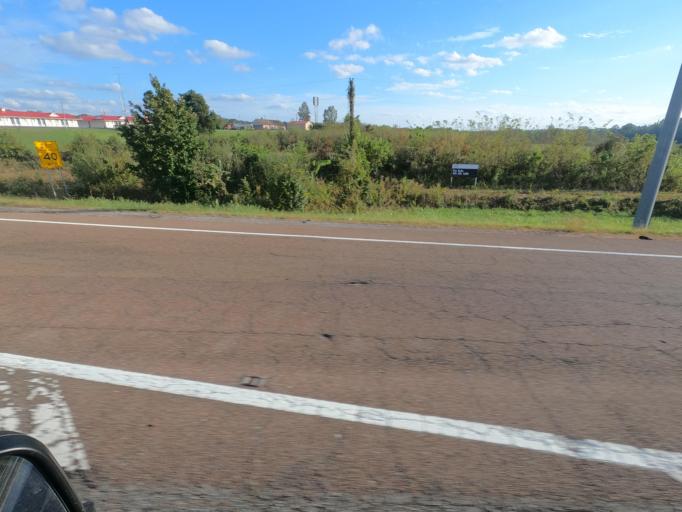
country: US
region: Tennessee
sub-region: Henderson County
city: Lexington
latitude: 35.7885
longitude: -88.3944
